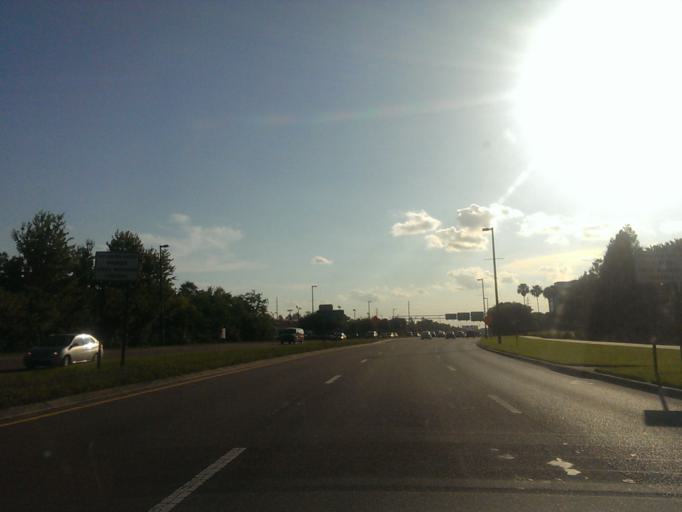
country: US
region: Florida
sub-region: Osceola County
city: Celebration
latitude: 28.3573
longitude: -81.4925
